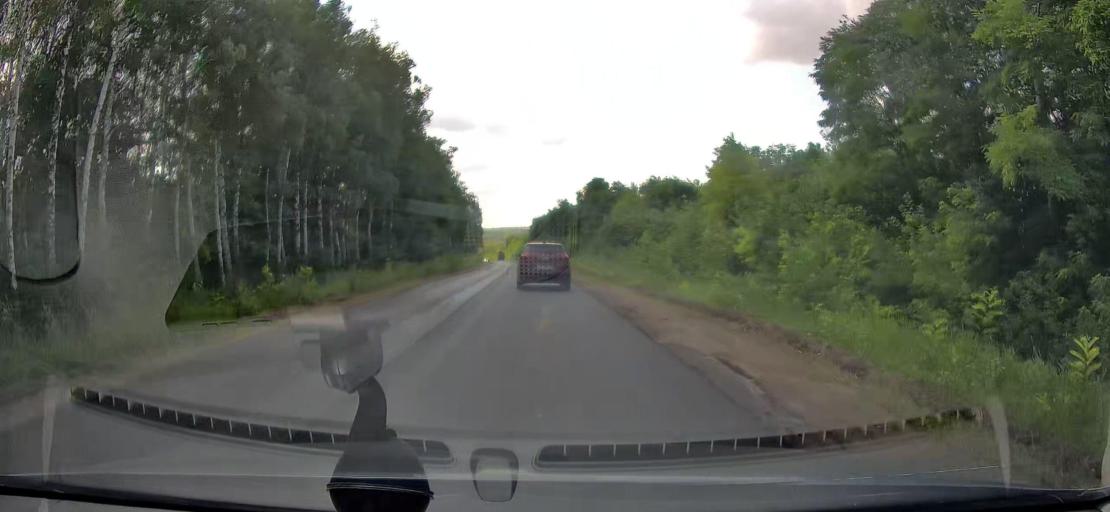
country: RU
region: Kursk
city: Zolotukhino
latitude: 51.9677
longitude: 36.2815
